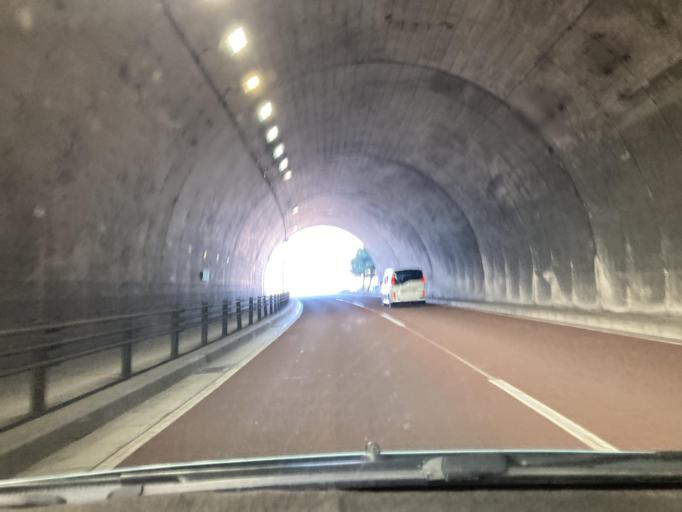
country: JP
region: Okinawa
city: Ginowan
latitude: 26.2503
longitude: 127.7492
